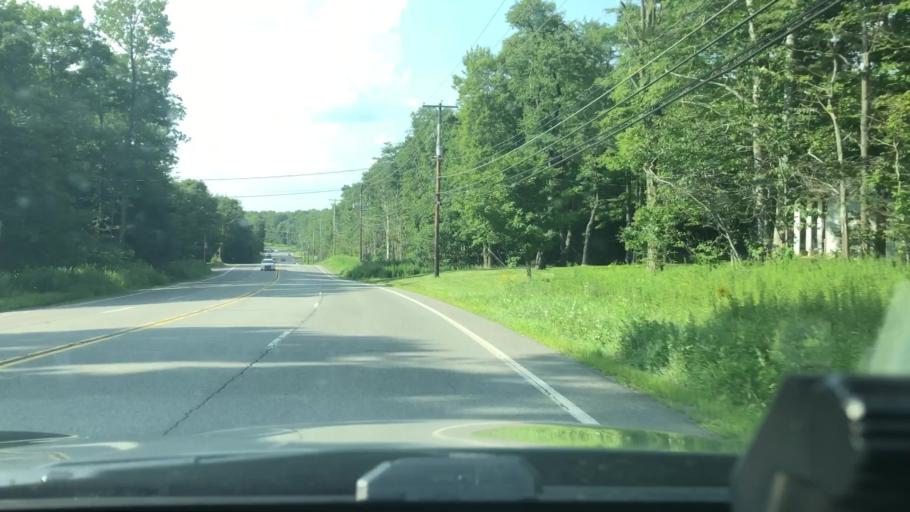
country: US
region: Pennsylvania
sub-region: Lackawanna County
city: Moscow
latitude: 41.2750
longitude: -75.5062
